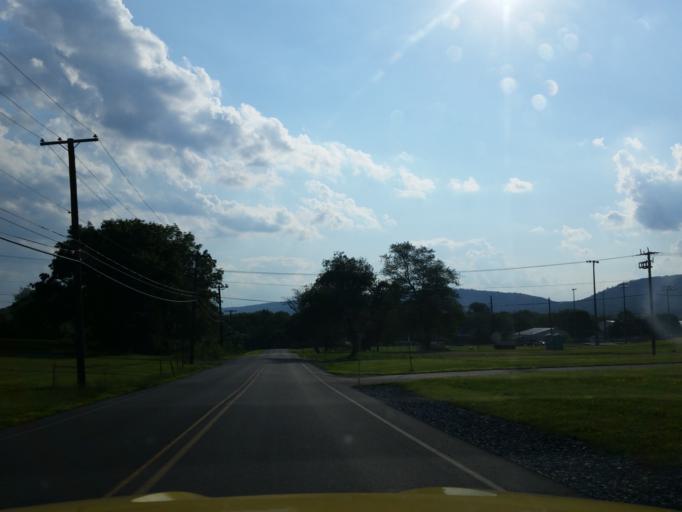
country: US
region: Pennsylvania
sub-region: Lebanon County
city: Jonestown
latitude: 40.4338
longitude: -76.5521
